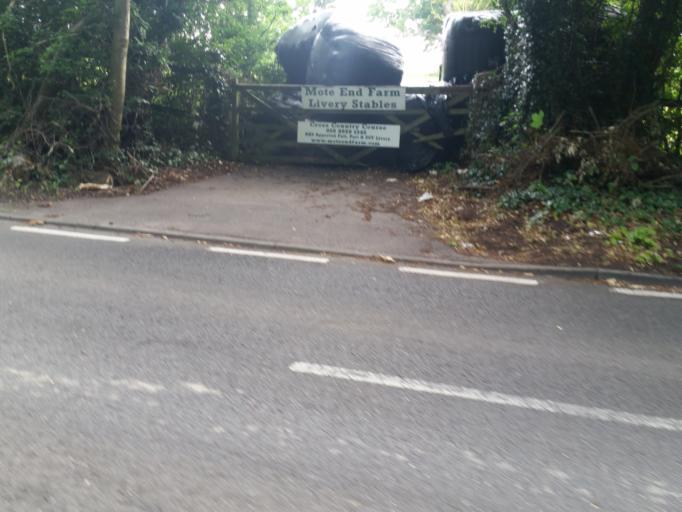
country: GB
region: England
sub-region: Greater London
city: High Barnet
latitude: 51.6337
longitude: -0.2363
